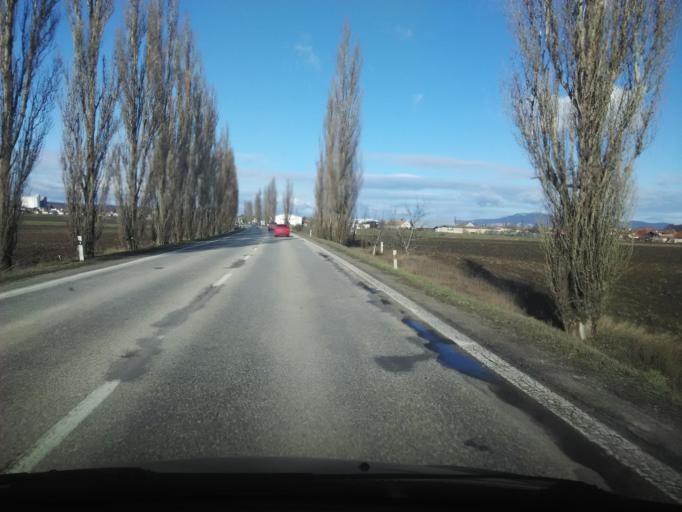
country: SK
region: Nitriansky
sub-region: Okres Nitra
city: Nitra
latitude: 48.2262
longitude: 18.1359
